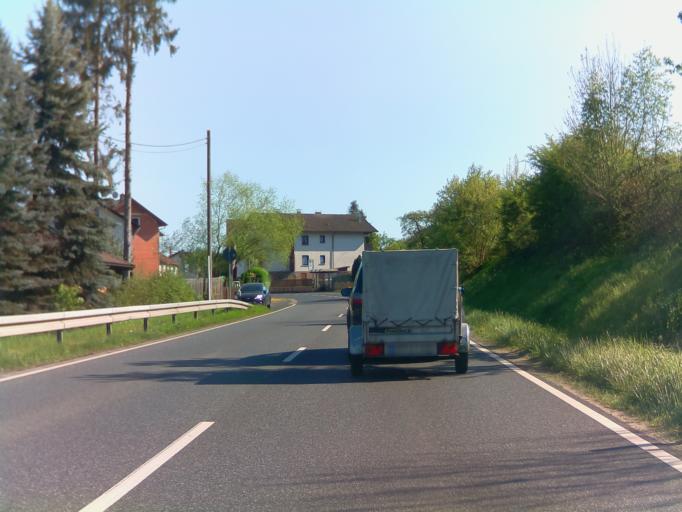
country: DE
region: Hesse
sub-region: Regierungsbezirk Darmstadt
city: Wachtersbach
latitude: 50.2784
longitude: 9.3061
